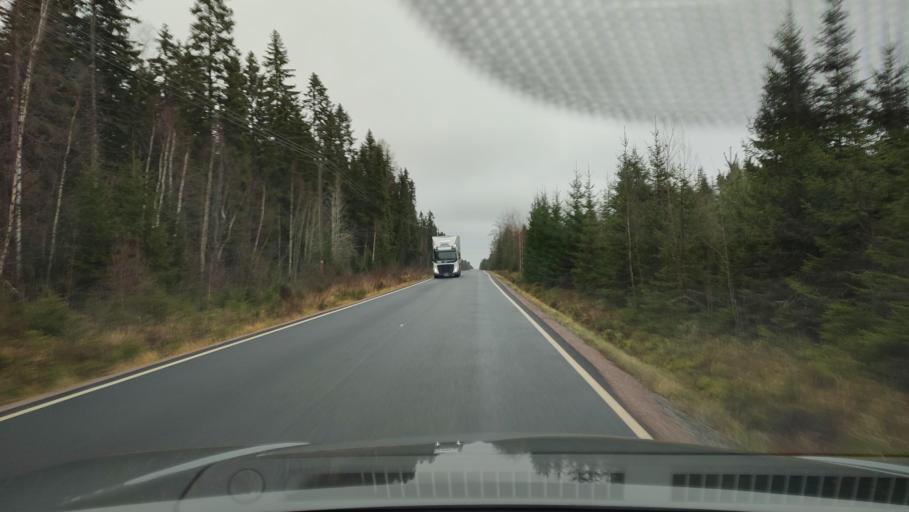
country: FI
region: Southern Ostrobothnia
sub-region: Suupohja
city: Karijoki
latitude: 62.1559
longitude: 21.7165
